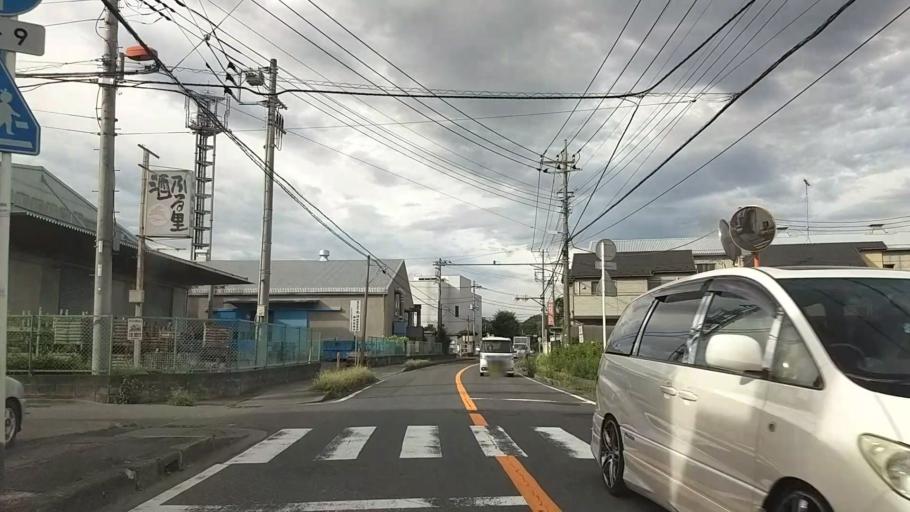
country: JP
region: Tokyo
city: Hachioji
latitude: 35.5669
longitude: 139.3409
